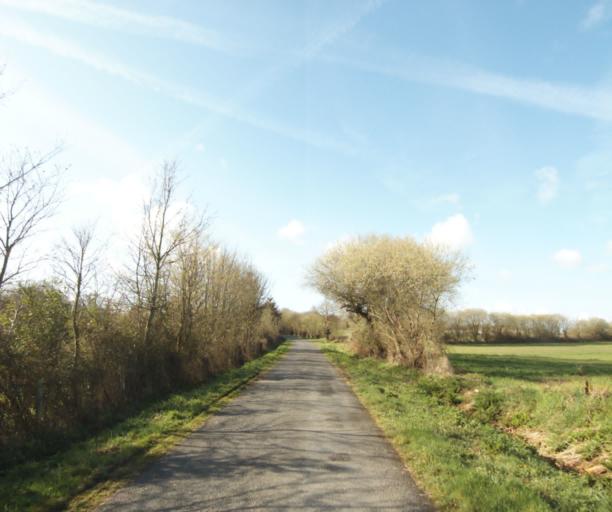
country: FR
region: Pays de la Loire
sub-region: Departement de la Loire-Atlantique
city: Bouvron
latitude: 47.4079
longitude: -1.8481
